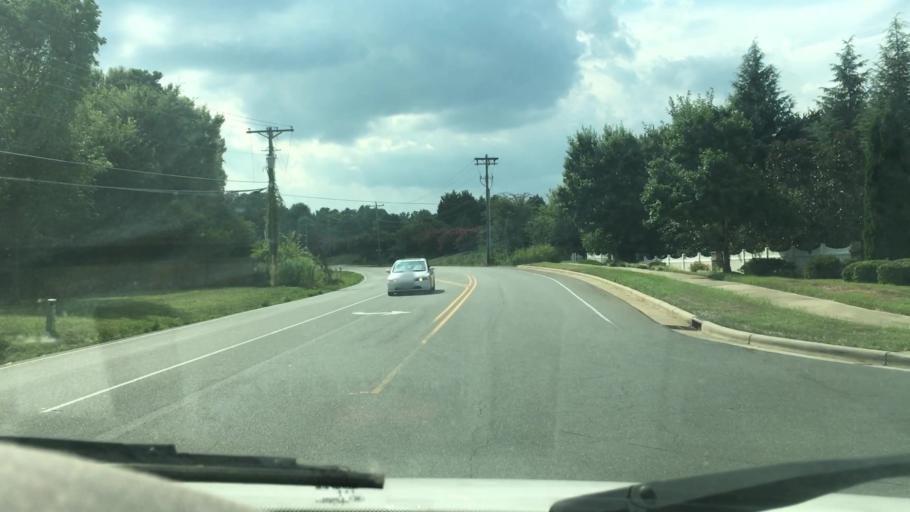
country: US
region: North Carolina
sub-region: Mecklenburg County
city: Huntersville
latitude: 35.4156
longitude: -80.8297
